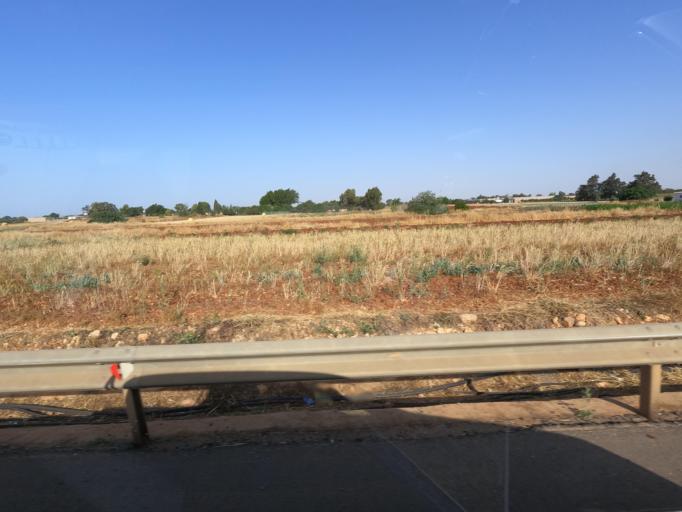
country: CY
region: Ammochostos
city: Liopetri
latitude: 34.9902
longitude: 33.9314
